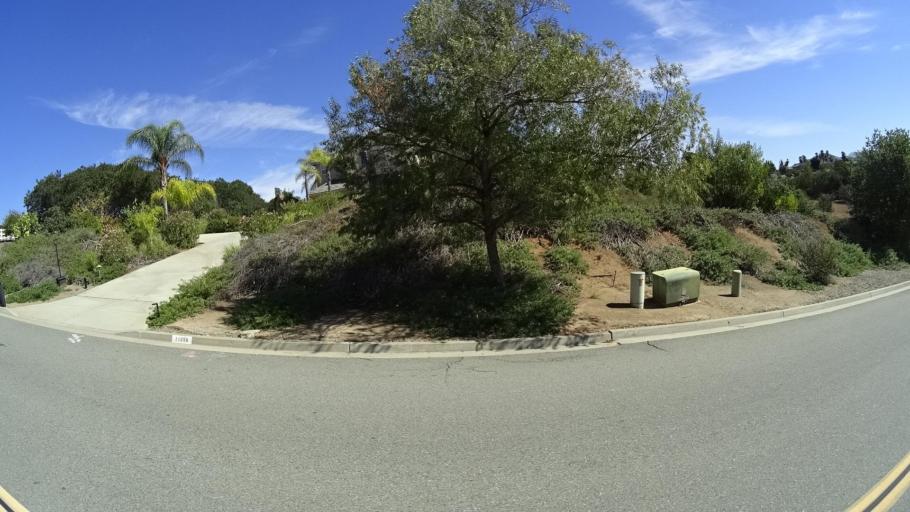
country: US
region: California
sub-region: San Diego County
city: Harbison Canyon
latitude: 32.8761
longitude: -116.8448
